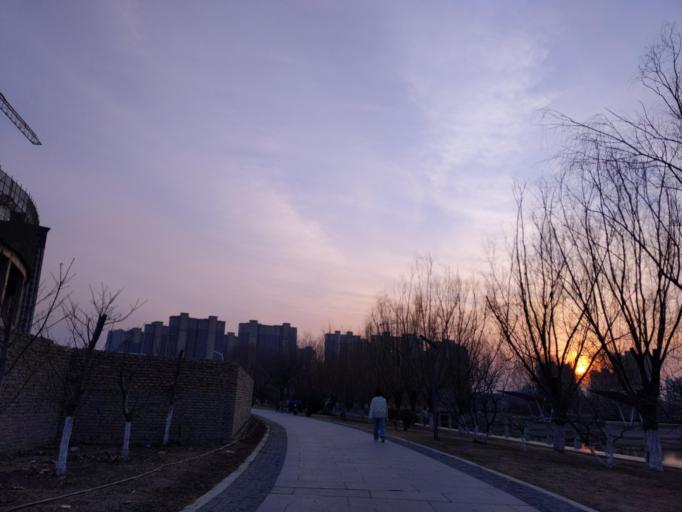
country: CN
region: Henan Sheng
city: Zhongyuanlu
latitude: 35.7766
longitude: 115.1284
